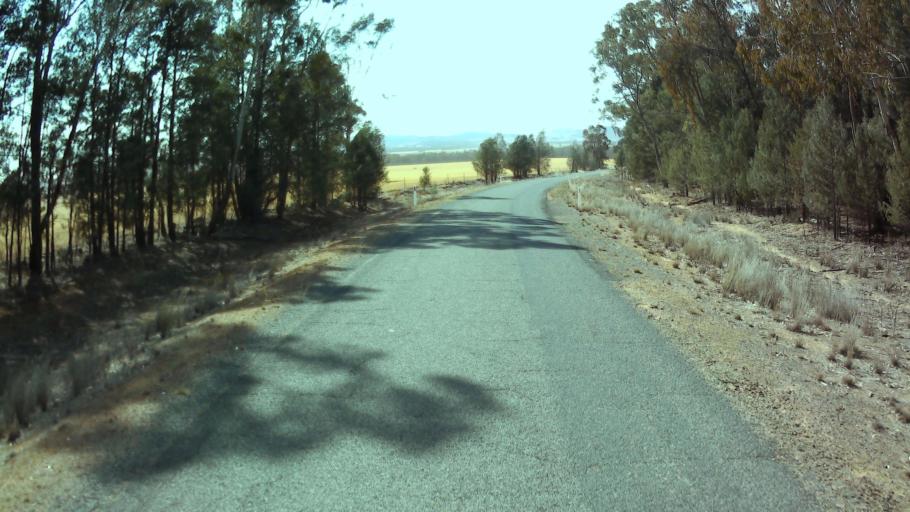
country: AU
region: New South Wales
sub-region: Weddin
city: Grenfell
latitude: -33.7511
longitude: 148.0668
